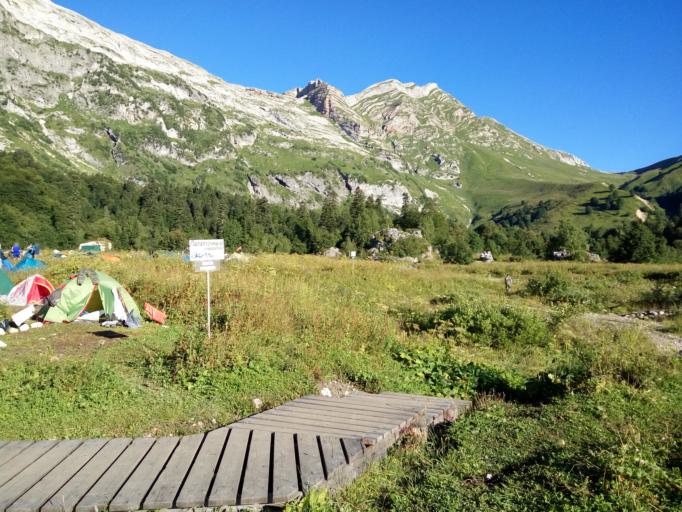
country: RU
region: Krasnodarskiy
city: Dagomys
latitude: 43.9598
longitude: 39.9308
